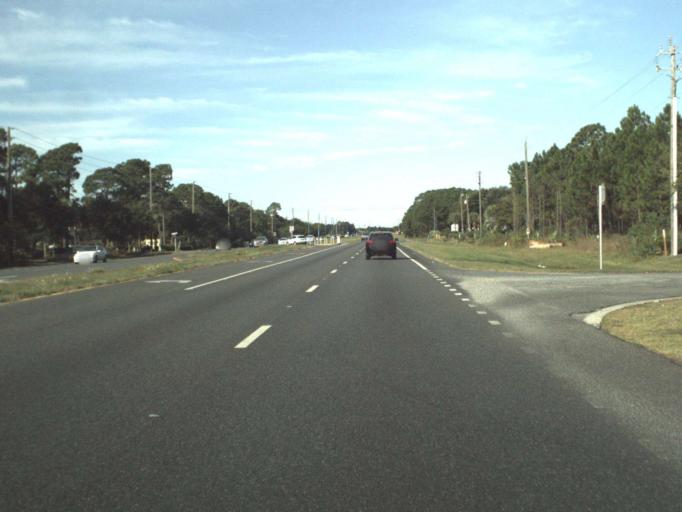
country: US
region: Florida
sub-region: Walton County
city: Miramar Beach
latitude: 30.3853
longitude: -86.3851
